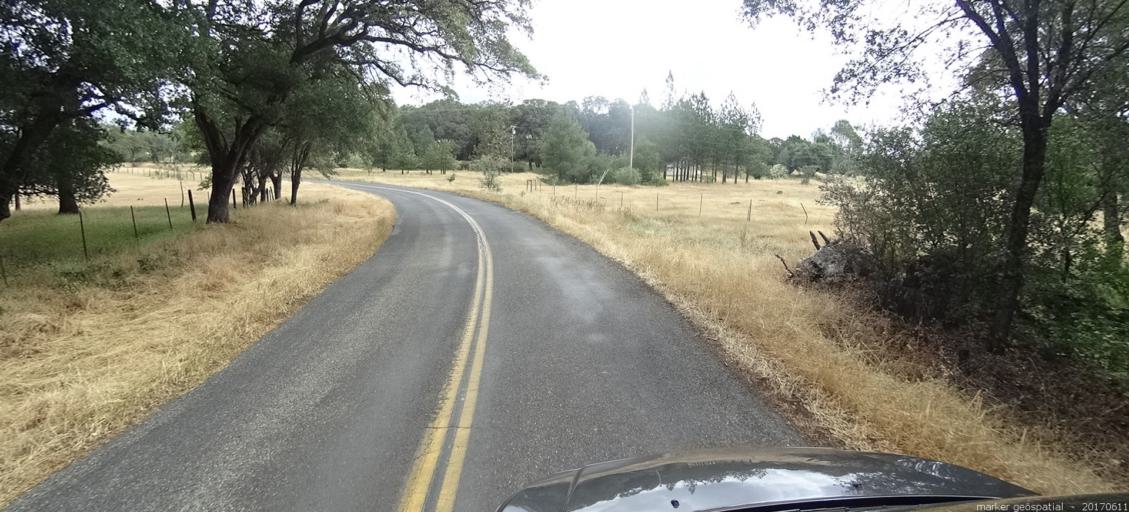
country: US
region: California
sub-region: Butte County
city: Oroville
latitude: 39.6057
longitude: -121.5296
